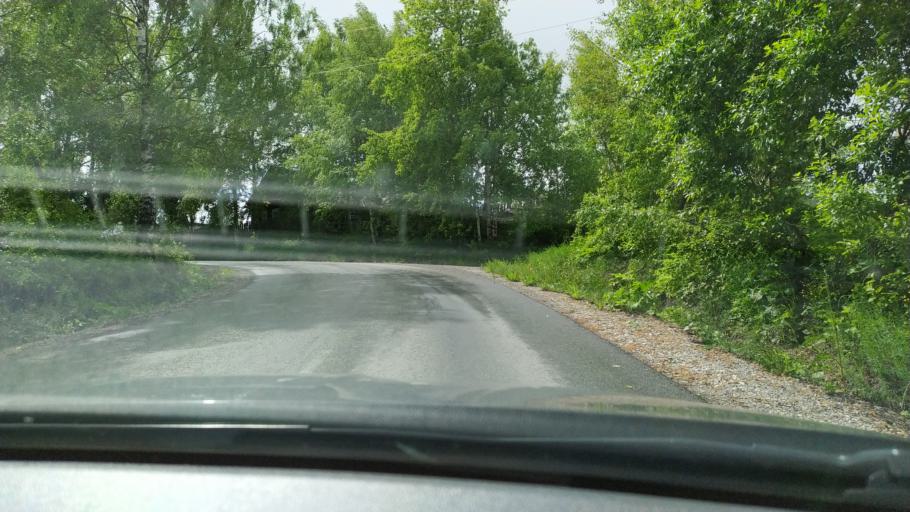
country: RU
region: Perm
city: Gremyachinsk
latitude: 58.5128
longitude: 57.8343
